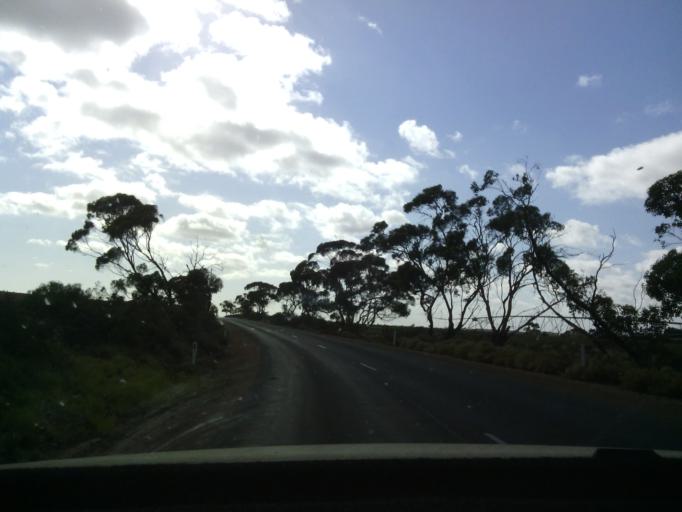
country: AU
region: South Australia
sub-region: Berri and Barmera
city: Berri
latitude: -34.2565
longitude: 140.5990
